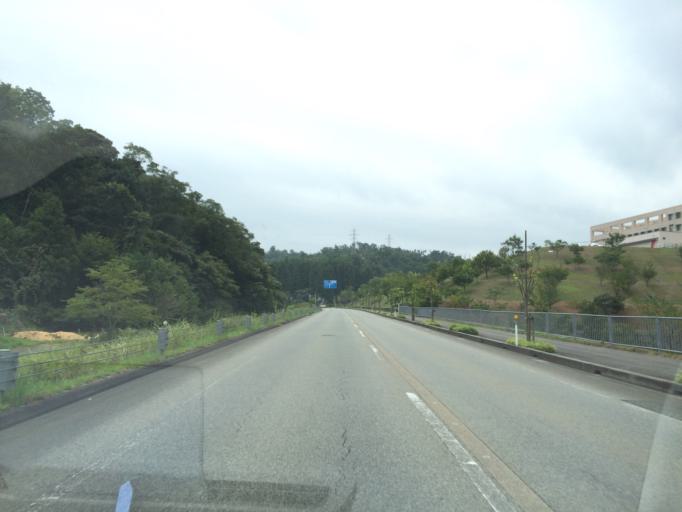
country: JP
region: Hyogo
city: Toyooka
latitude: 35.5287
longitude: 134.8087
